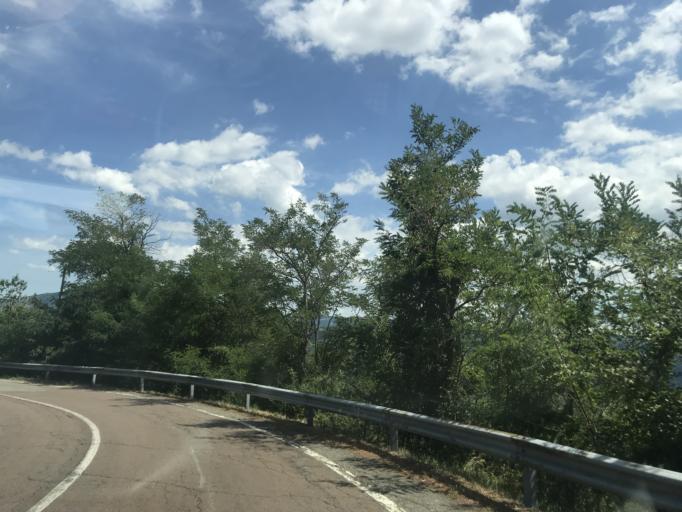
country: IT
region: Emilia-Romagna
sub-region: Provincia di Bologna
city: Grizzana
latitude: 44.2556
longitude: 11.1610
